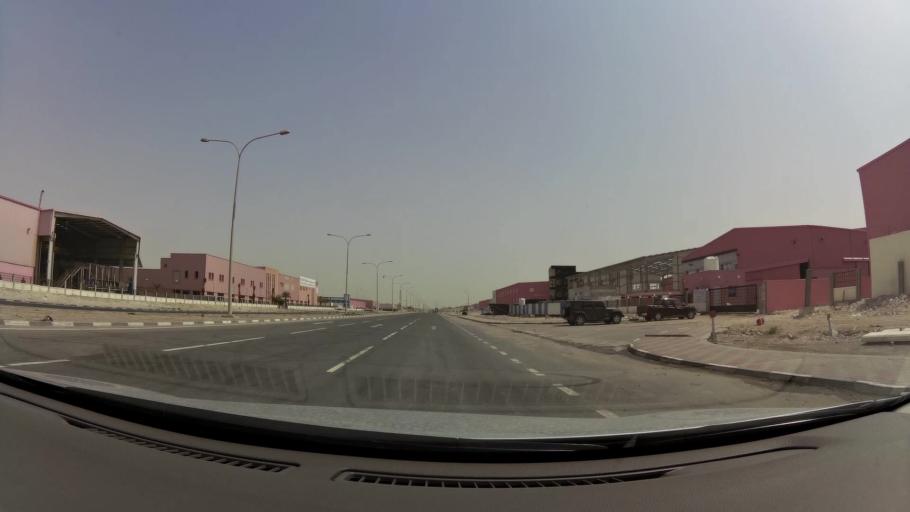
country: QA
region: Al Wakrah
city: Al Wukayr
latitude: 25.1518
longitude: 51.3958
